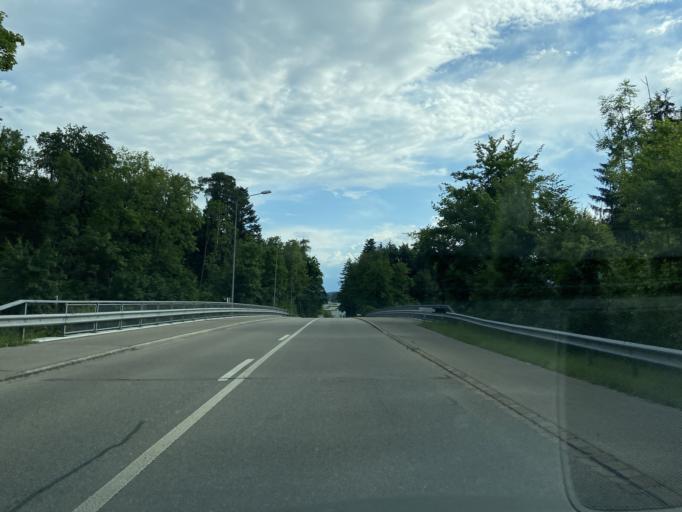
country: CH
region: Zurich
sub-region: Bezirk Winterthur
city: Veltheim
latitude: 47.5250
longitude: 8.7228
